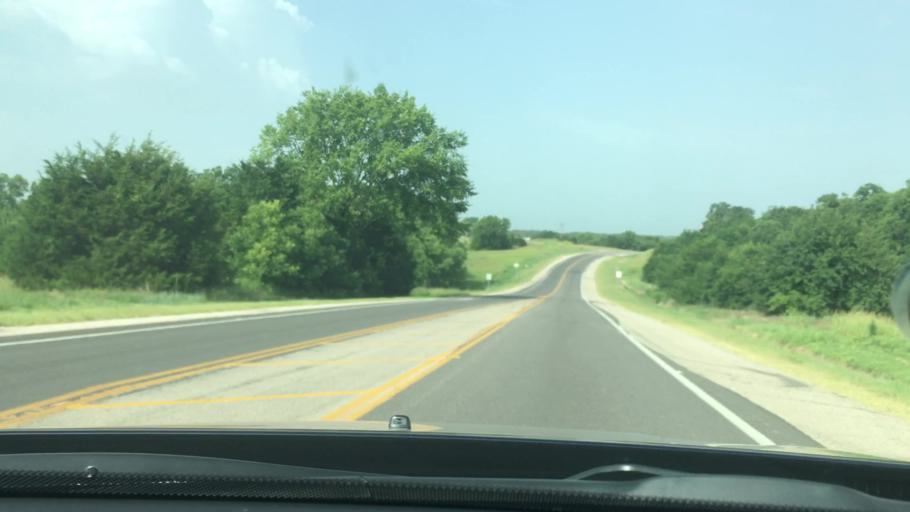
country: US
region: Oklahoma
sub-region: Pontotoc County
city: Ada
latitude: 34.7837
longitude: -96.7405
